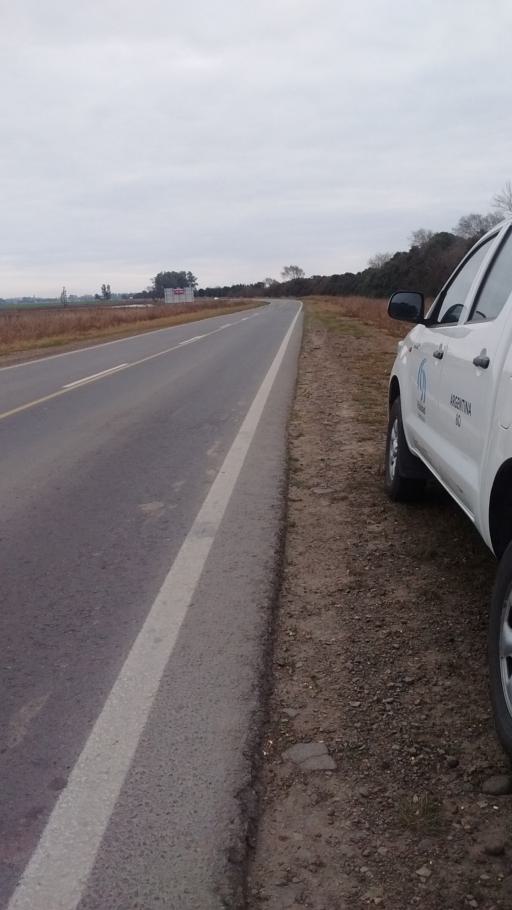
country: AR
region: Santa Fe
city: Las Rosas
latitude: -32.5254
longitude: -61.5513
